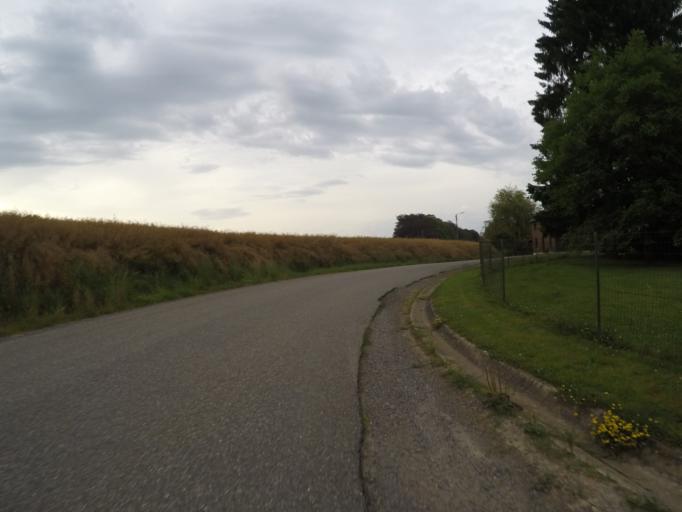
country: BE
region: Wallonia
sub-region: Province de Namur
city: Assesse
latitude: 50.3174
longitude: 5.0382
